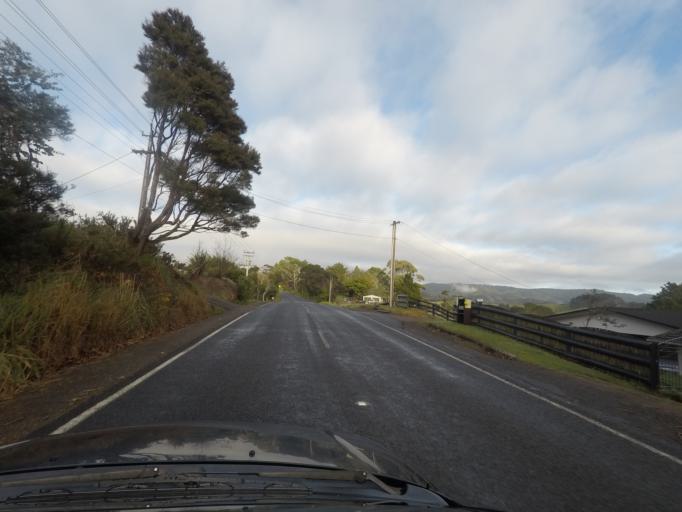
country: NZ
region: Auckland
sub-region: Auckland
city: Waitakere
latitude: -36.9116
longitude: 174.6077
